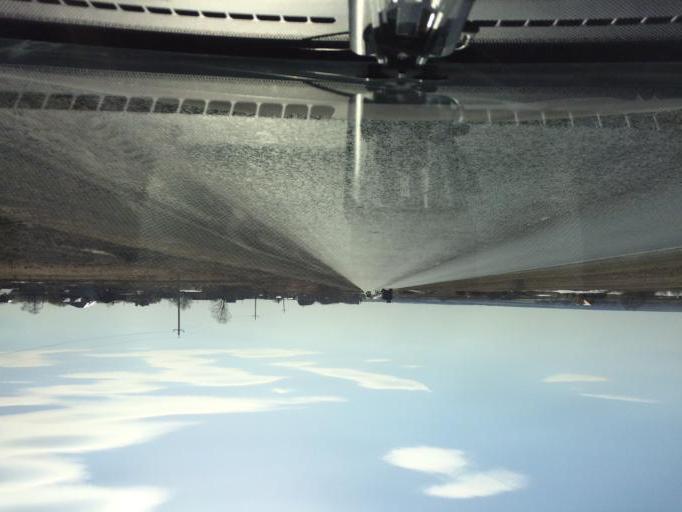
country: RU
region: Mariy-El
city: Yoshkar-Ola
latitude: 56.7142
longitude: 48.0916
